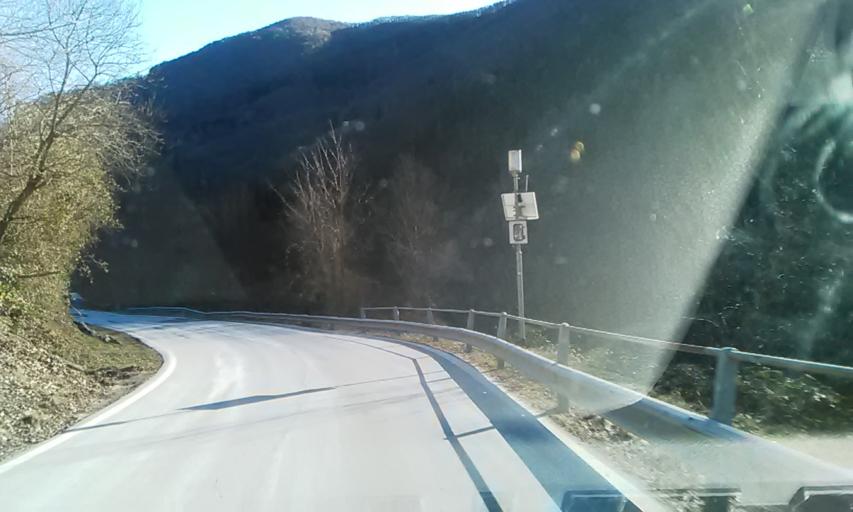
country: IT
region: Piedmont
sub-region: Provincia di Vercelli
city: Boccioleto
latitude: 45.8287
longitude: 8.1007
